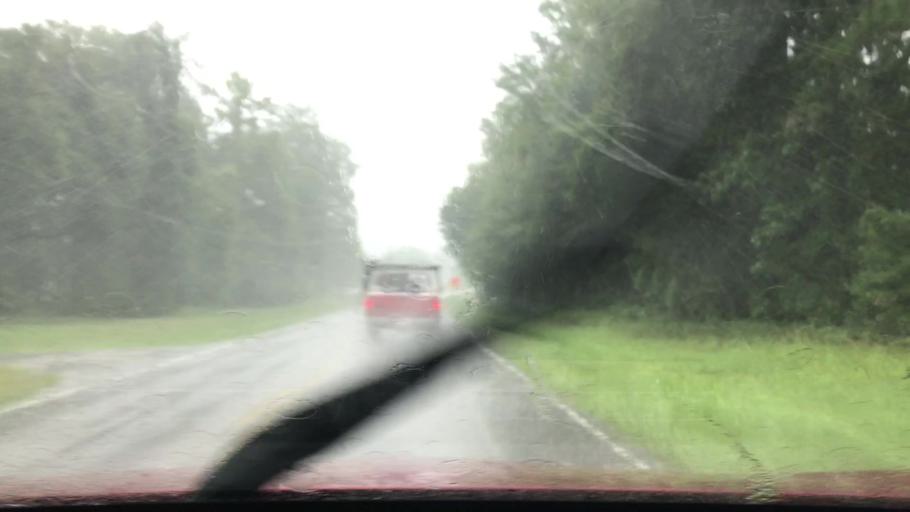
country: US
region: South Carolina
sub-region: Horry County
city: Red Hill
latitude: 33.8712
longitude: -78.9823
